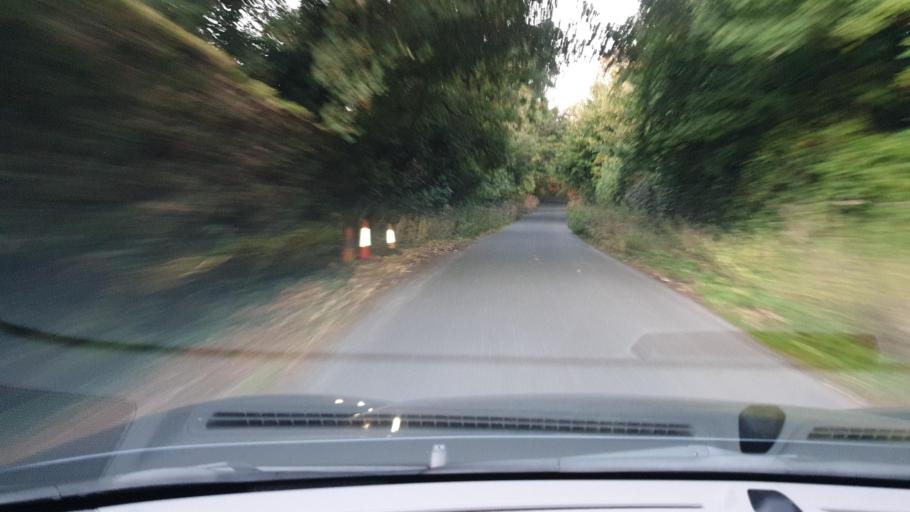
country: IE
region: Leinster
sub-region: Kildare
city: Prosperous
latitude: 53.3447
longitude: -6.7571
